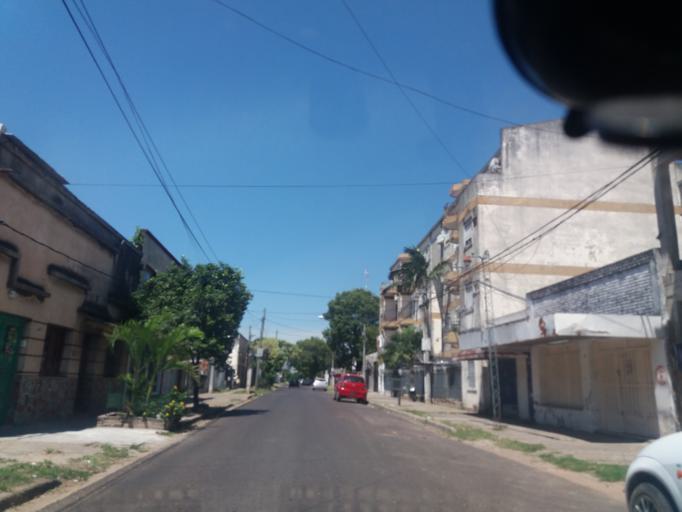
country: AR
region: Corrientes
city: Corrientes
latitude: -27.4811
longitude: -58.8452
